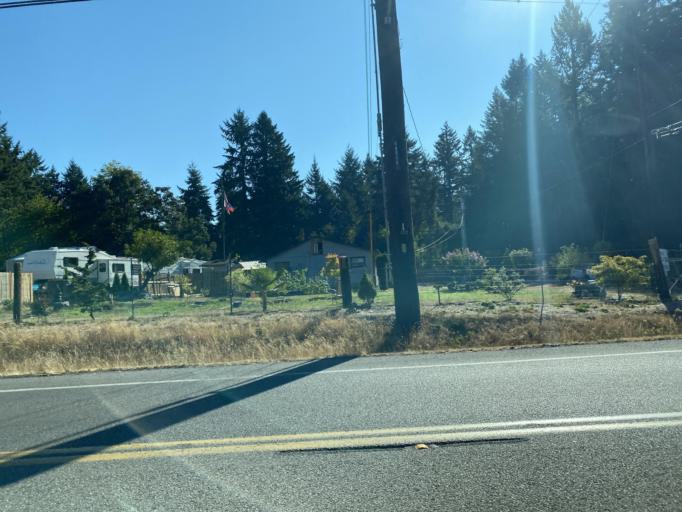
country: US
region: Washington
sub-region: Thurston County
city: Tanglewilde-Thompson Place
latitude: 47.0035
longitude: -122.7386
